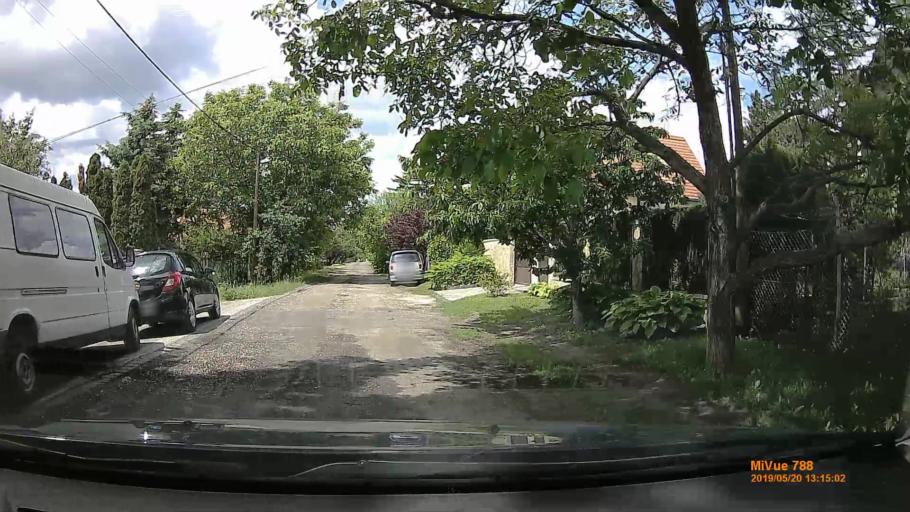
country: HU
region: Pest
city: Ecser
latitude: 47.4639
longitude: 19.3002
